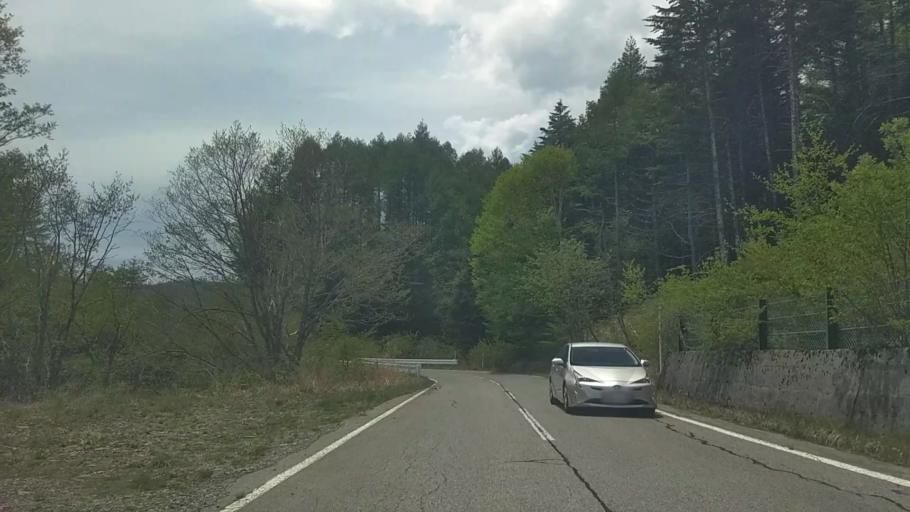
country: JP
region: Nagano
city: Saku
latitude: 36.0857
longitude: 138.3866
